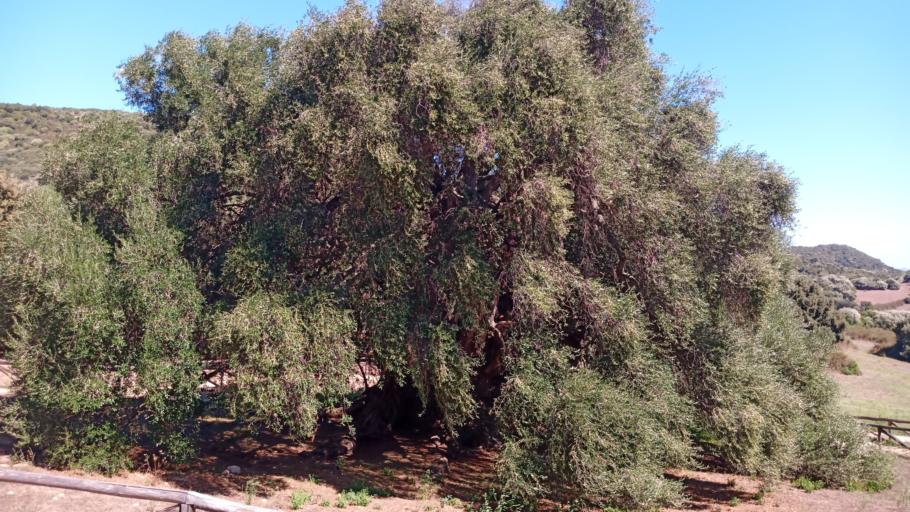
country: IT
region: Sardinia
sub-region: Provincia di Olbia-Tempio
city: Sant'Antonio di Gallura
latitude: 41.0064
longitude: 9.2549
